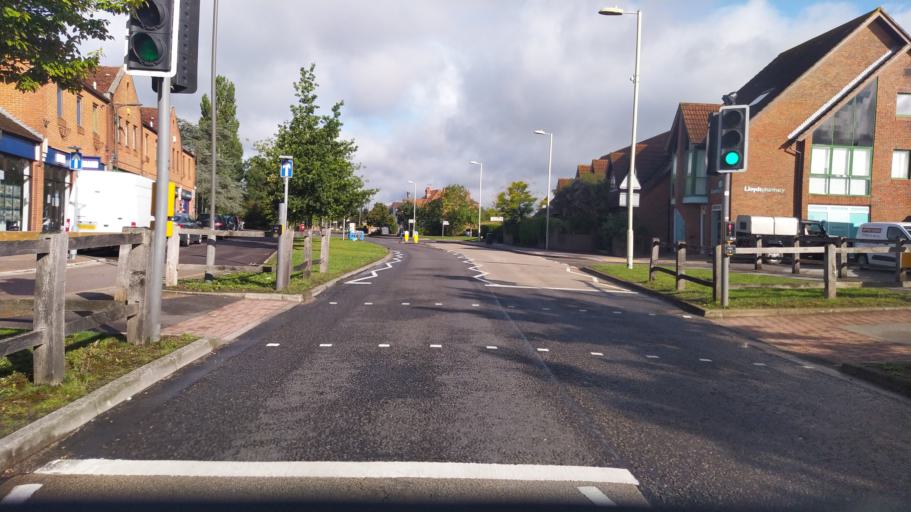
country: GB
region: England
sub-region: Hampshire
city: Totton
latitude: 50.9192
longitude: -1.4902
